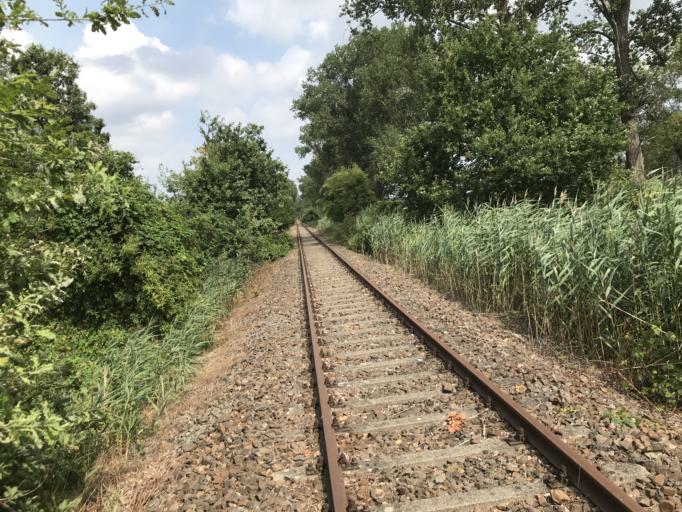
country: DE
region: Brandenburg
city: Sperenberg
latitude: 52.0743
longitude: 13.2879
